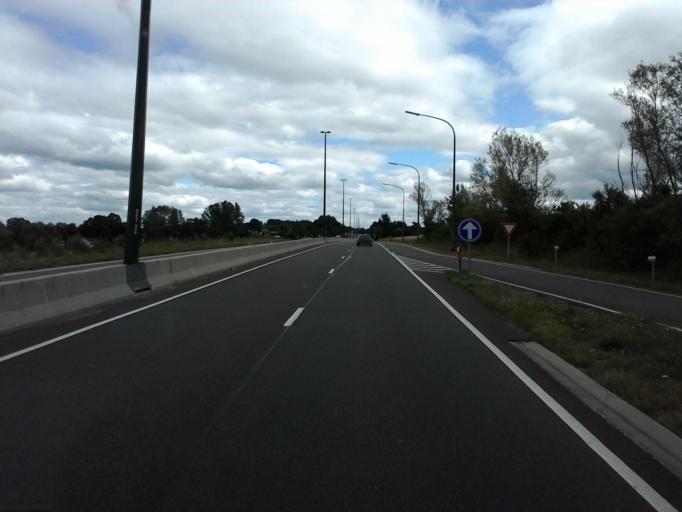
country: BE
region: Wallonia
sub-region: Province du Luxembourg
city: Attert
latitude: 49.7440
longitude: 5.7839
